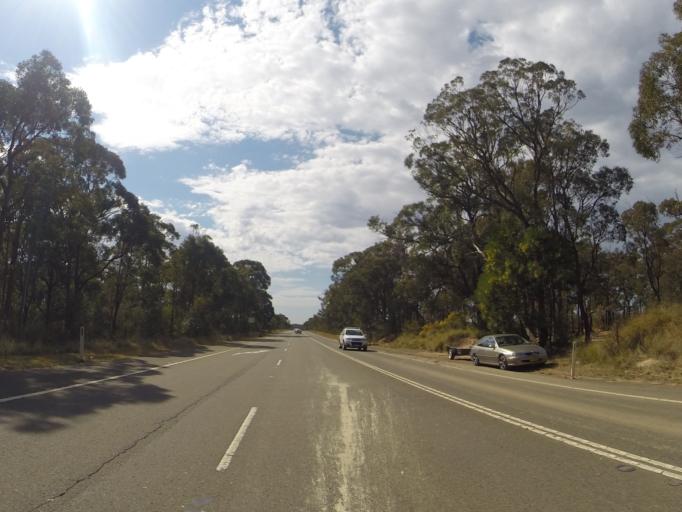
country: AU
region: New South Wales
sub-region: Liverpool
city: Holsworthy
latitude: -34.0200
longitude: 150.9766
